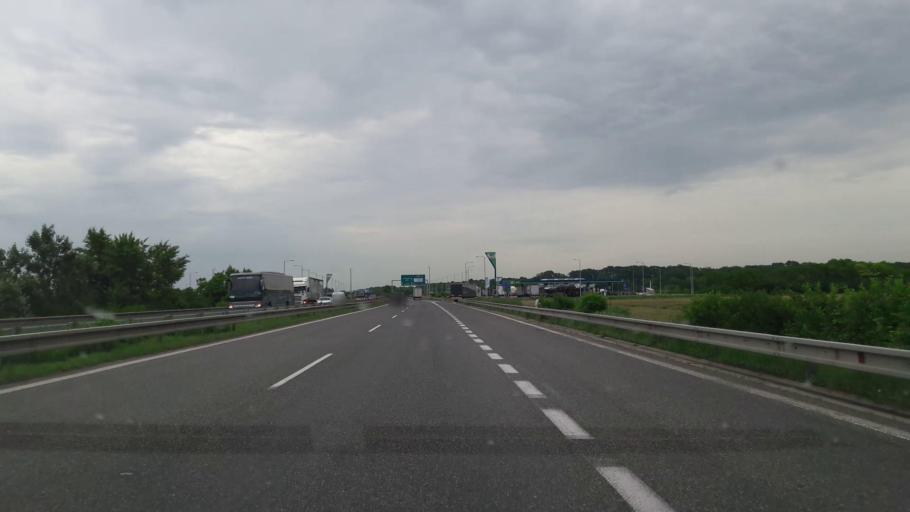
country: AT
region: Burgenland
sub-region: Politischer Bezirk Neusiedl am See
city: Kittsee
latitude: 48.0906
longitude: 17.0987
